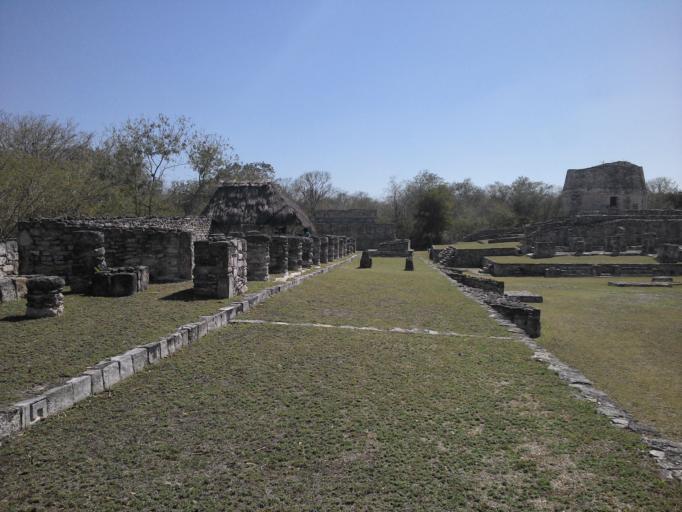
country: MX
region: Yucatan
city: Tekoh
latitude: 20.6301
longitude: -89.4600
